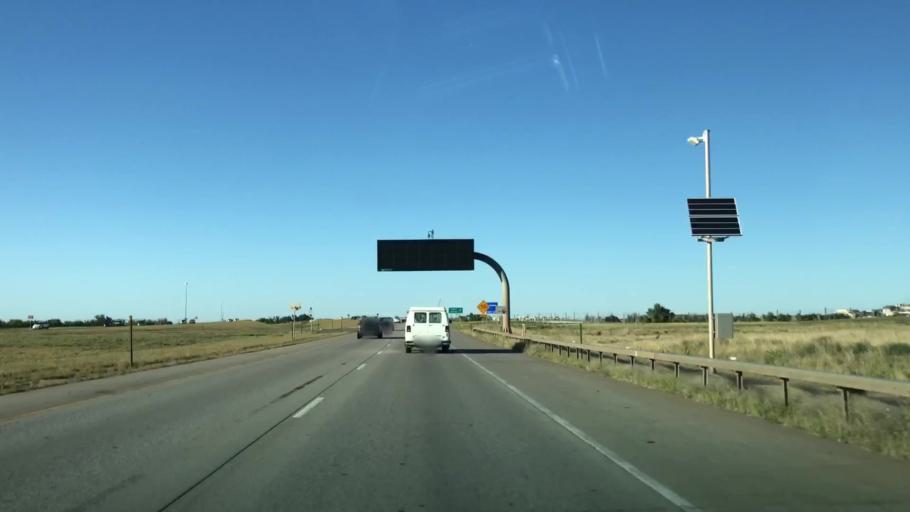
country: US
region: Colorado
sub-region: Adams County
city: Aurora
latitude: 39.7918
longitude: -104.7882
